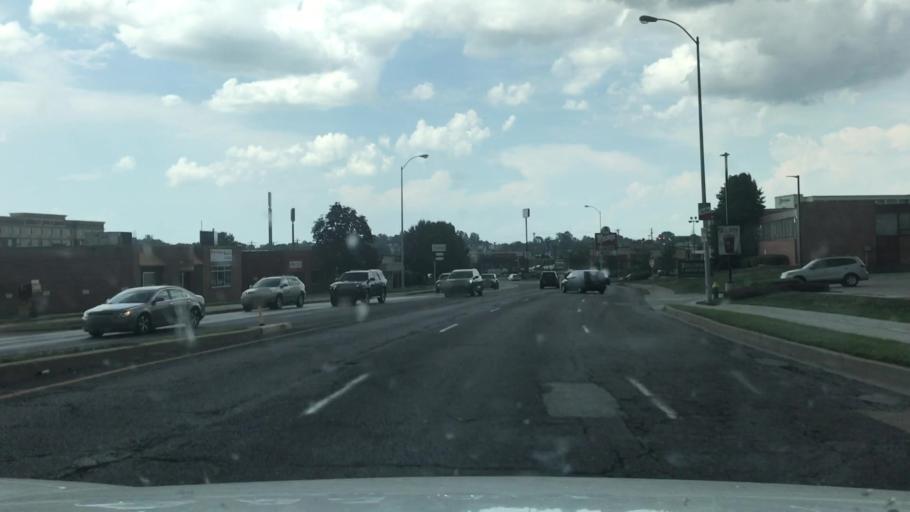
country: US
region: Missouri
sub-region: Saint Louis County
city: Richmond Heights
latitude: 38.6153
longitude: -90.2872
